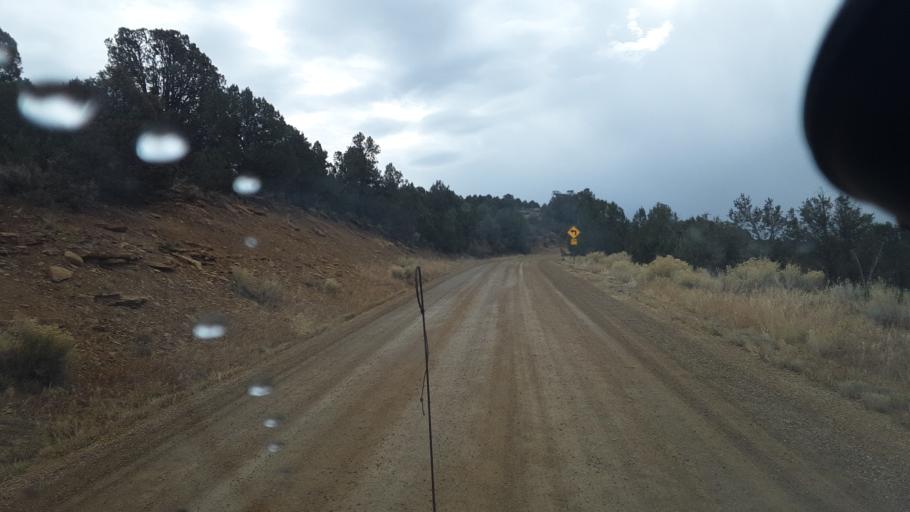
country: US
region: Colorado
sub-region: Montezuma County
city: Mancos
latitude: 37.2007
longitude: -108.1375
